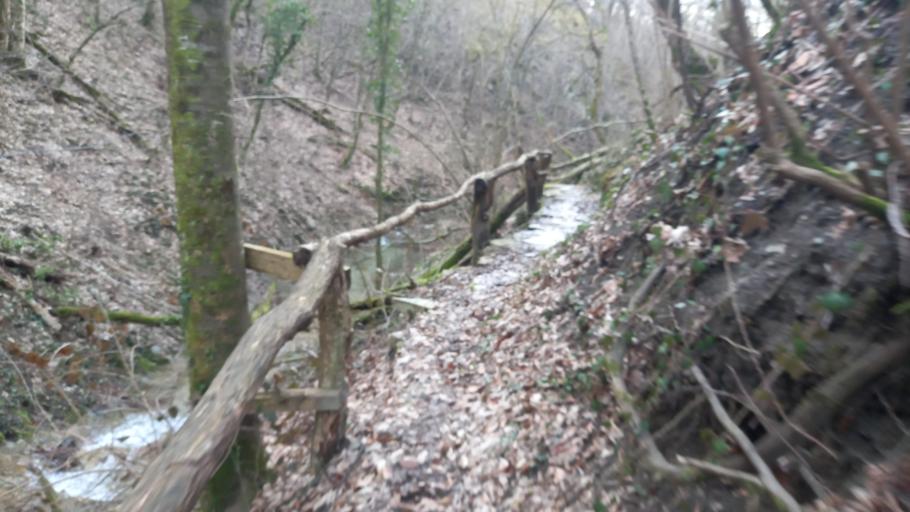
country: RU
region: Krasnodarskiy
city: Pshada
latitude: 44.5138
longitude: 38.4040
